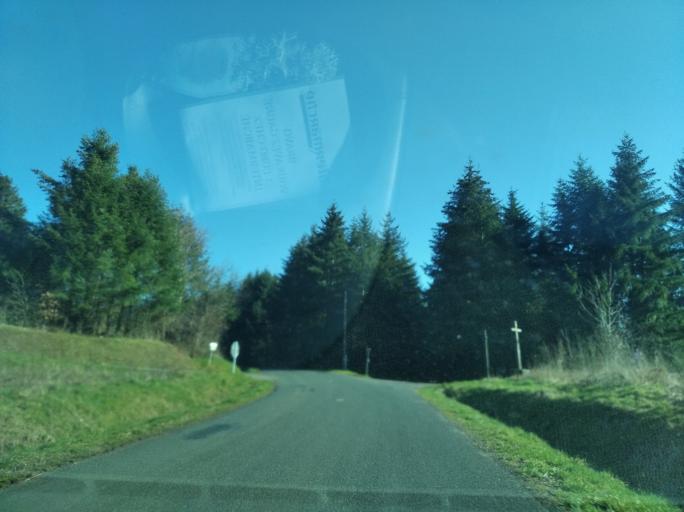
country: FR
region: Auvergne
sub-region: Departement de l'Allier
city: Le Mayet-de-Montagne
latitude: 46.1019
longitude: 3.6926
